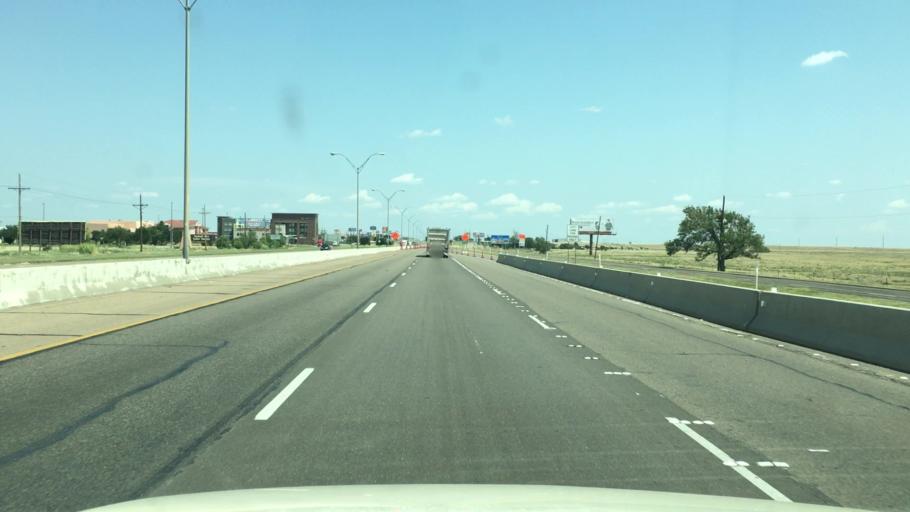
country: US
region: Texas
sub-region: Potter County
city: Amarillo
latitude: 35.1927
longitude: -101.7376
